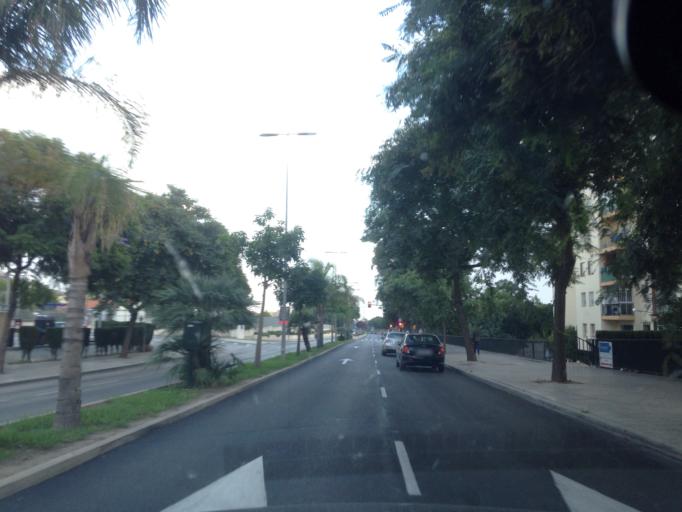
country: ES
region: Andalusia
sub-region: Provincia de Malaga
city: Malaga
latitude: 36.7304
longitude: -4.4681
